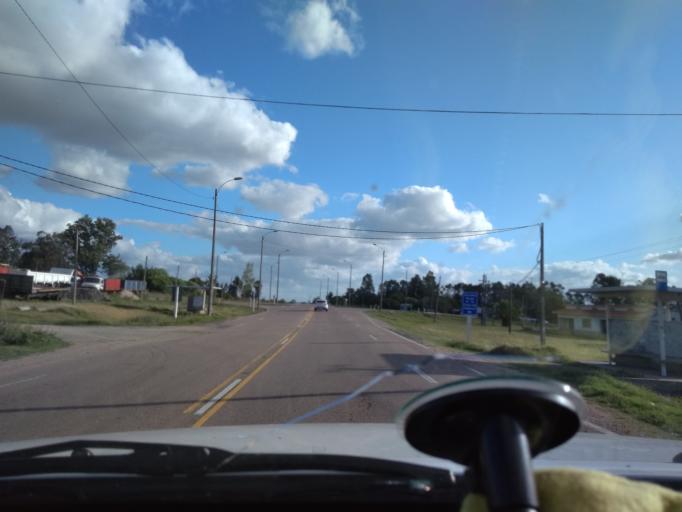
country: UY
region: Canelones
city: Tala
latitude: -34.3899
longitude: -55.7991
